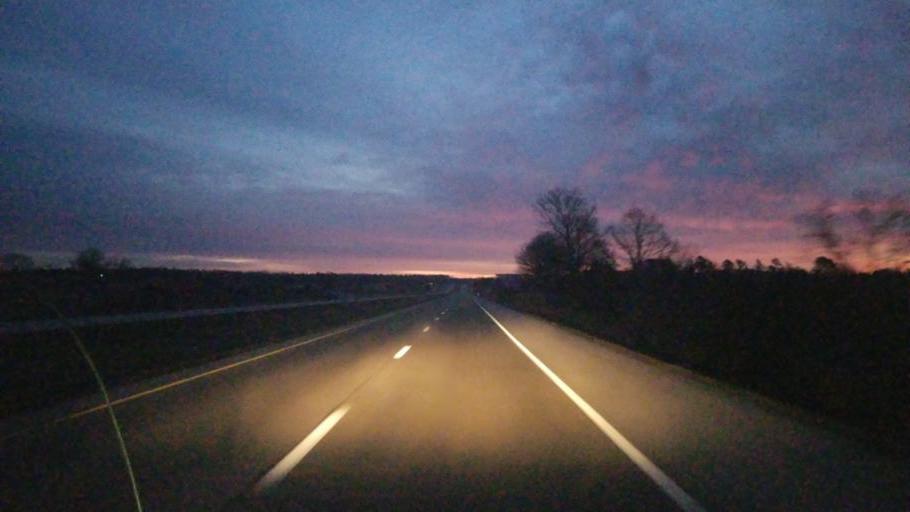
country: US
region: Missouri
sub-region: Howell County
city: Mountain View
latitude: 36.9932
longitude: -91.5161
